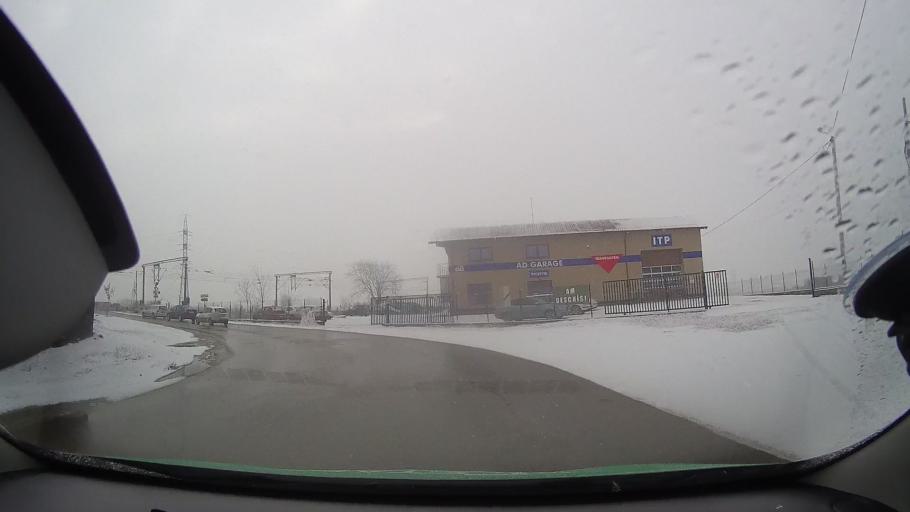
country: RO
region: Alba
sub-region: Municipiul Aiud
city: Aiud
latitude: 46.3059
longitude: 23.7330
